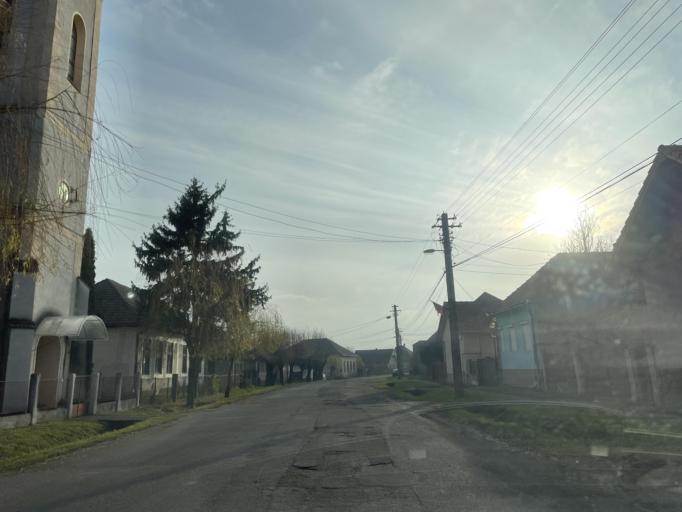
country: RO
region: Mures
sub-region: Municipiul Reghin
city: Apalina
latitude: 46.7474
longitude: 24.6938
